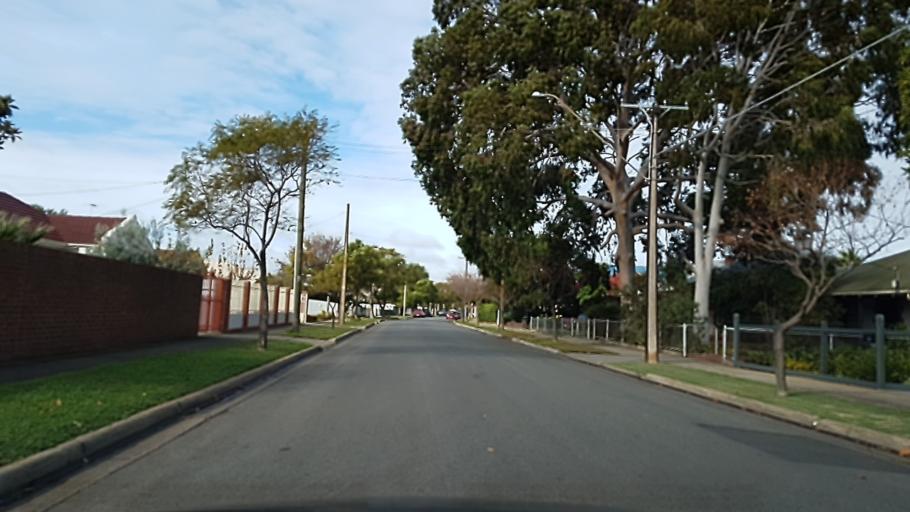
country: AU
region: South Australia
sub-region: Charles Sturt
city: Woodville
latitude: -34.8778
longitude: 138.5466
